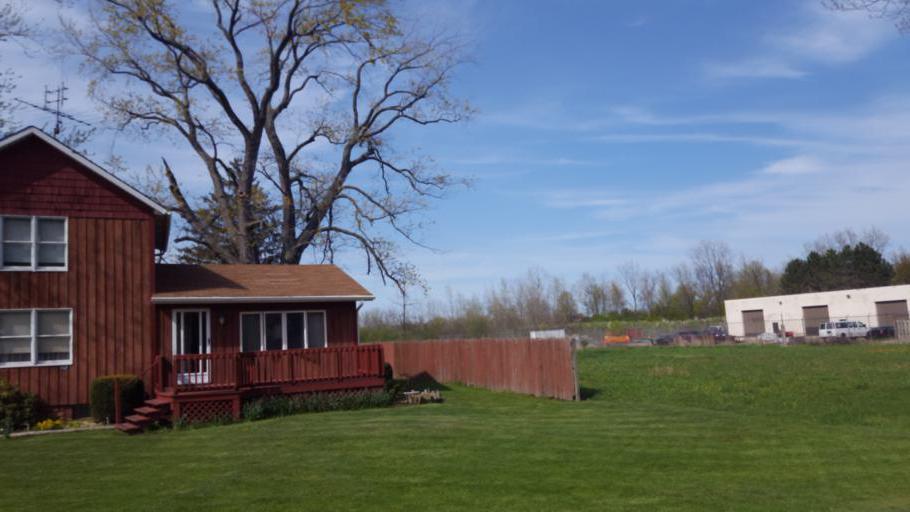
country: US
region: Ohio
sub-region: Lake County
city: Painesville
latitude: 41.7475
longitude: -81.2197
